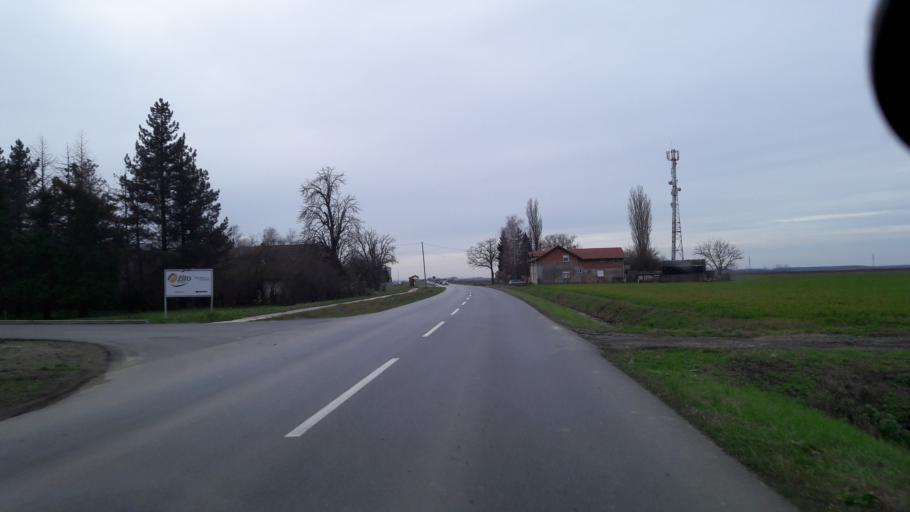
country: HR
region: Osjecko-Baranjska
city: Ovcara
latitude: 45.5050
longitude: 18.5625
